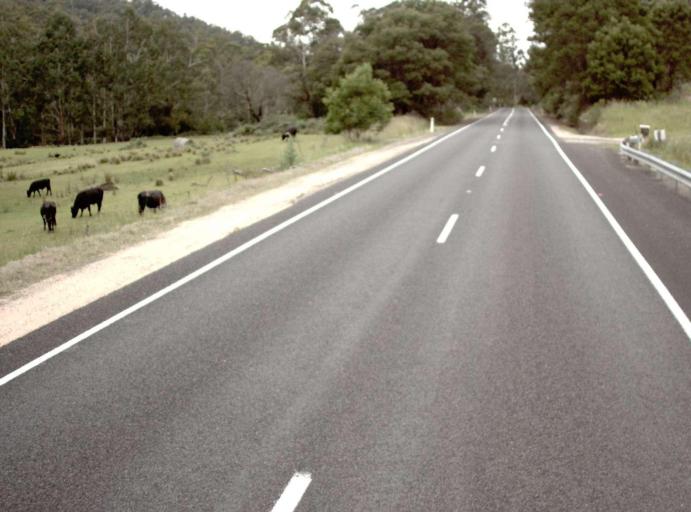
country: AU
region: New South Wales
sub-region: Bombala
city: Bombala
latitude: -37.4135
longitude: 149.1980
